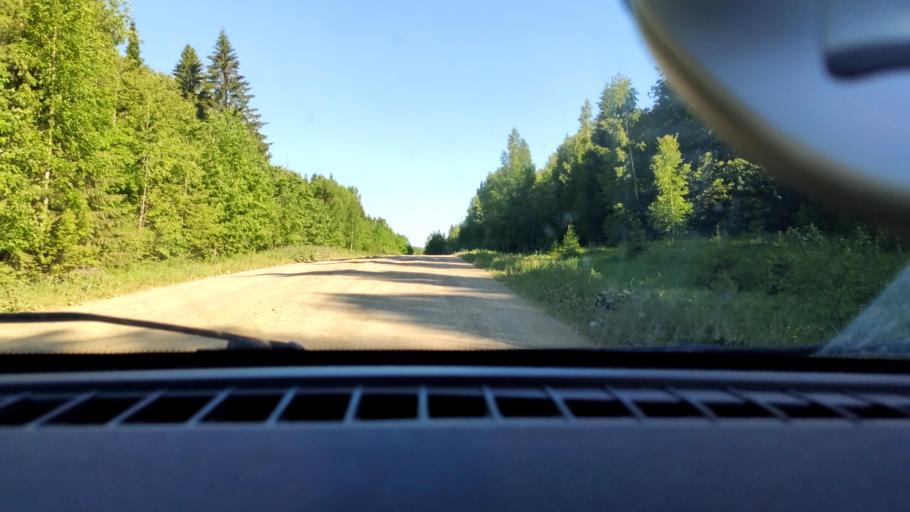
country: RU
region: Perm
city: Novyye Lyady
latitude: 58.1841
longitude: 56.5842
